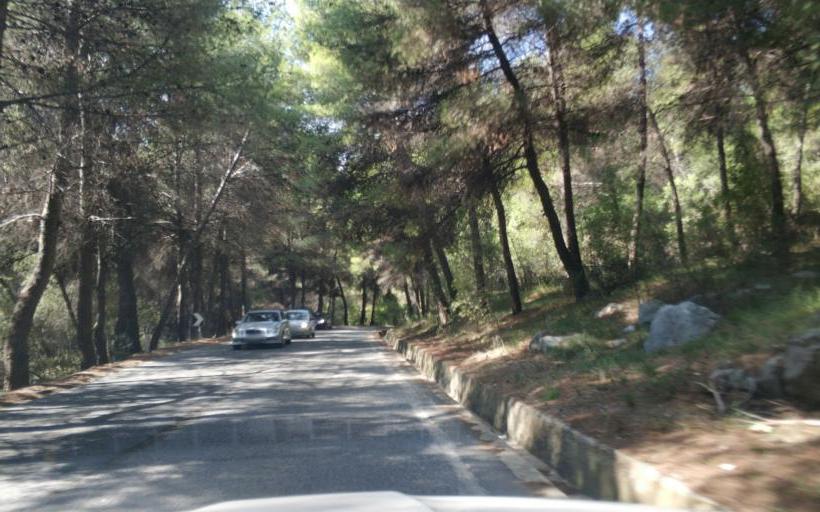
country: AL
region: Durres
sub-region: Rrethi i Krujes
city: Kruje
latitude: 41.4920
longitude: 19.7683
